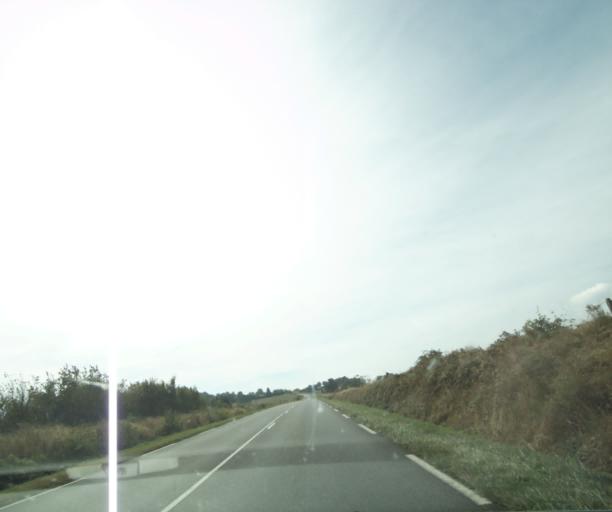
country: FR
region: Auvergne
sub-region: Departement de l'Allier
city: Le Donjon
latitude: 46.3145
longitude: 3.7707
